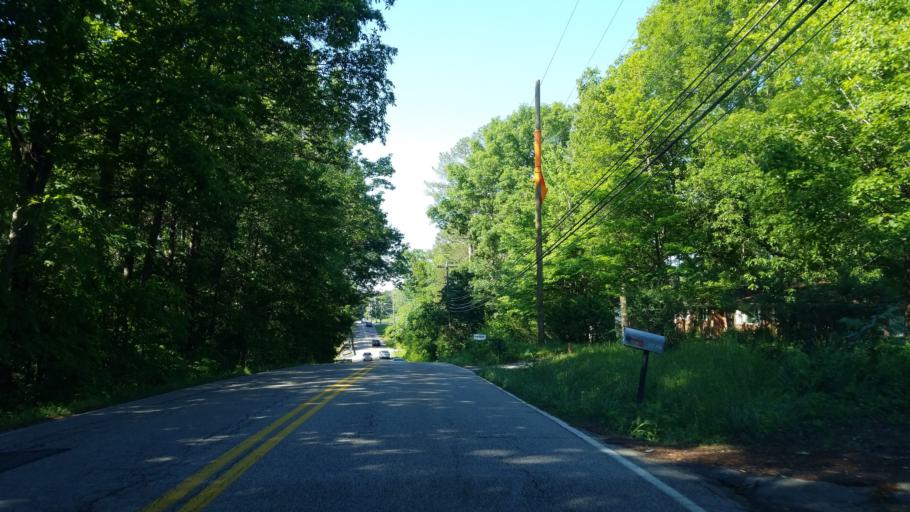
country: US
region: Tennessee
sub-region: Hamilton County
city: East Brainerd
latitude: 35.0384
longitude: -85.1317
